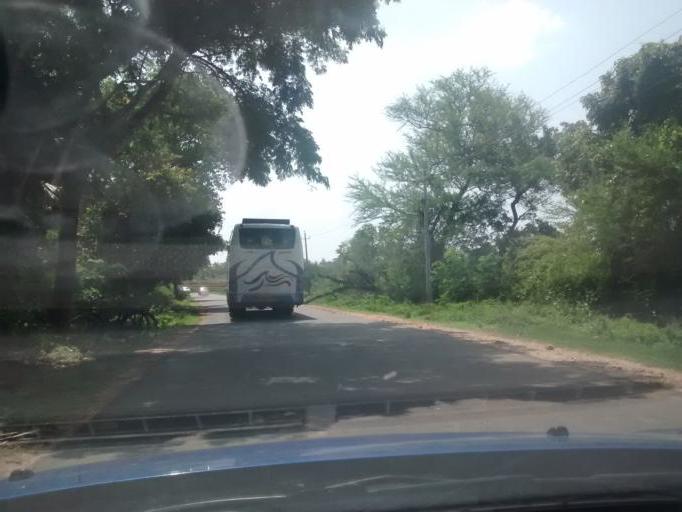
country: IN
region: Karnataka
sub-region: Hassan
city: Konanur
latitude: 12.5816
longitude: 76.1842
